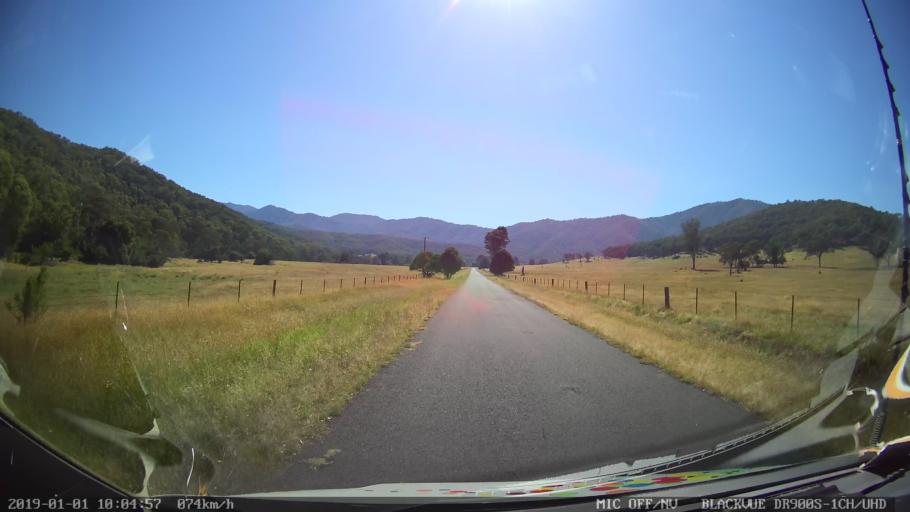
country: AU
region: New South Wales
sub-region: Snowy River
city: Jindabyne
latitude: -36.1746
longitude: 148.1292
